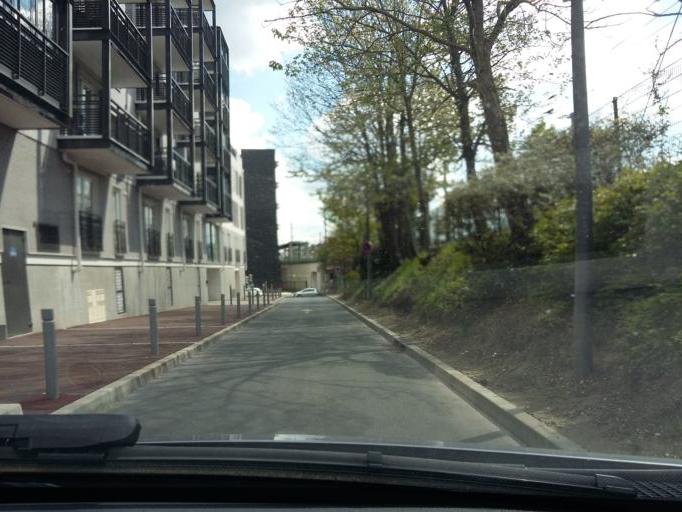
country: FR
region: Ile-de-France
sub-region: Departement du Val-d'Oise
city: Ermont
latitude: 48.9813
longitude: 2.2693
